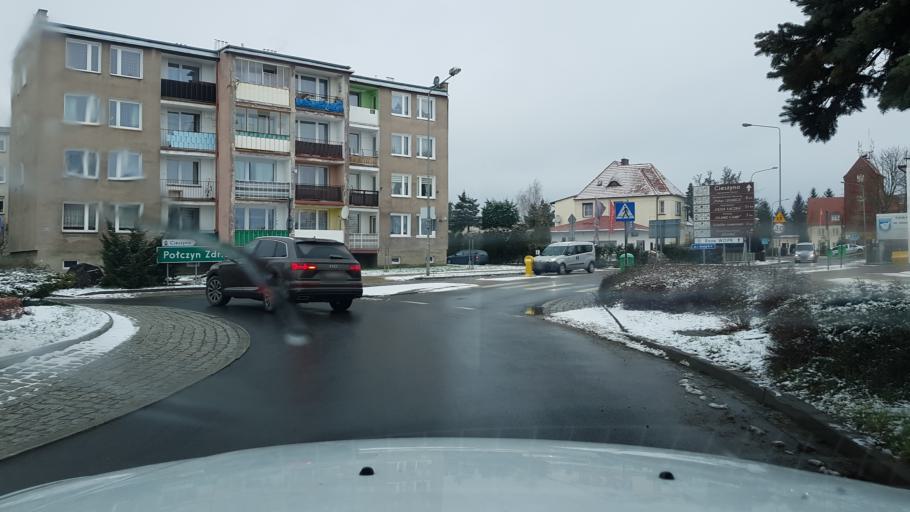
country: PL
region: West Pomeranian Voivodeship
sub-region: Powiat drawski
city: Zlocieniec
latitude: 53.5337
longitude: 16.0161
